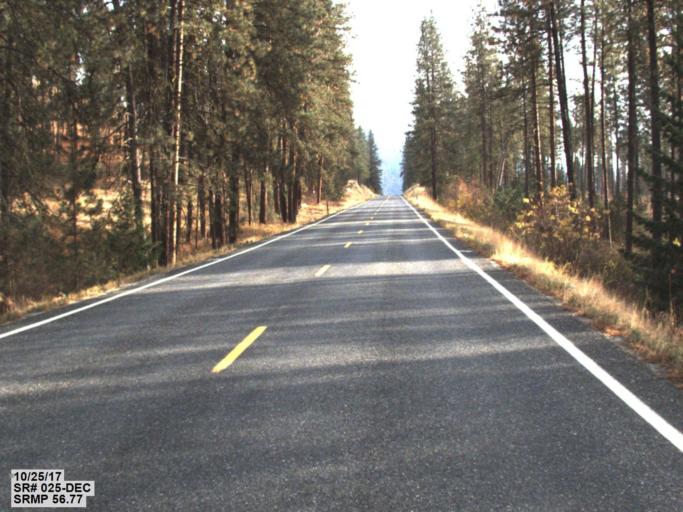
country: US
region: Washington
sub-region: Stevens County
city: Kettle Falls
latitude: 48.2943
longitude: -118.1436
